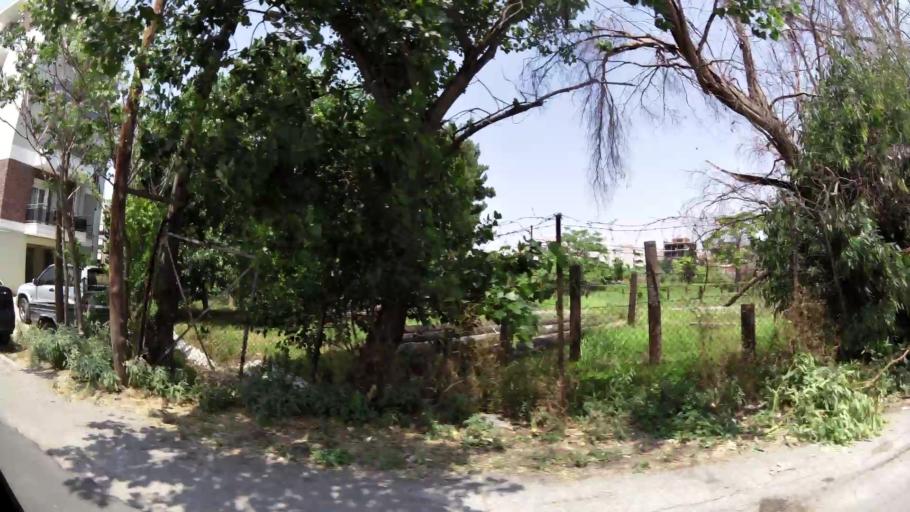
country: GR
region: Central Macedonia
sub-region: Nomos Thessalonikis
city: Menemeni
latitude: 40.6646
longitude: 22.9021
